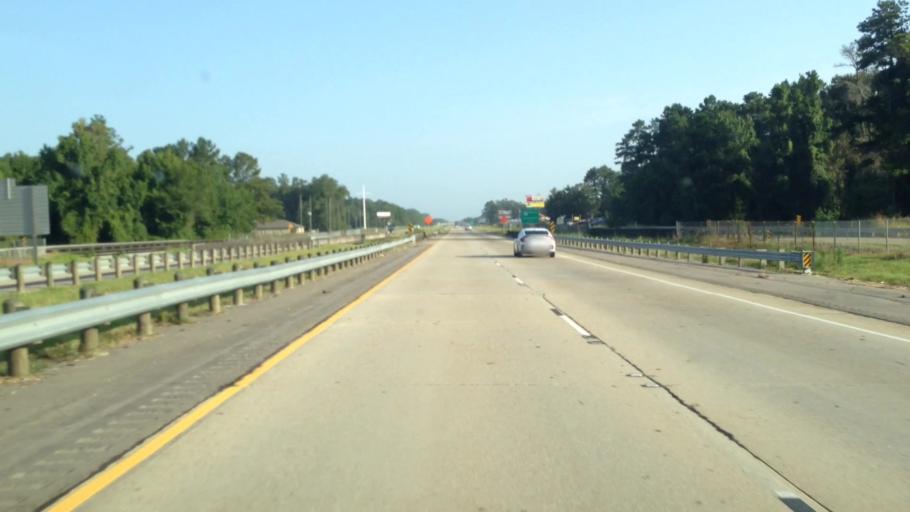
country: US
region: Louisiana
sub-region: Tangipahoa Parish
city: Ponchatoula
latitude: 30.4541
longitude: -90.4715
